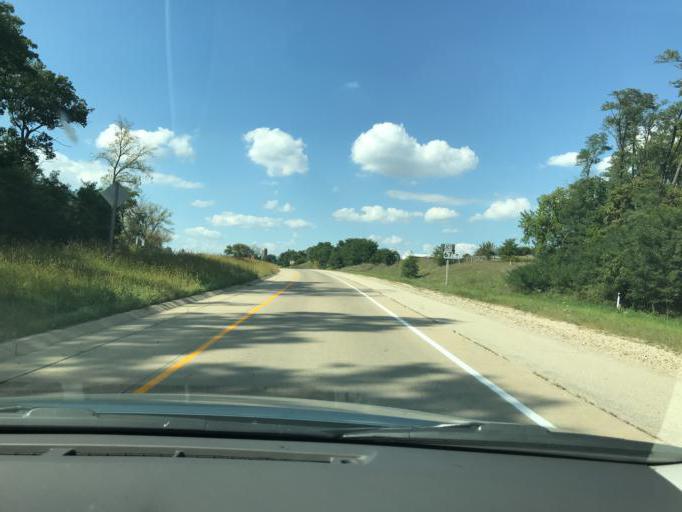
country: US
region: Wisconsin
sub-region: Walworth County
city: Williams Bay
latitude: 42.5965
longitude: -88.5369
